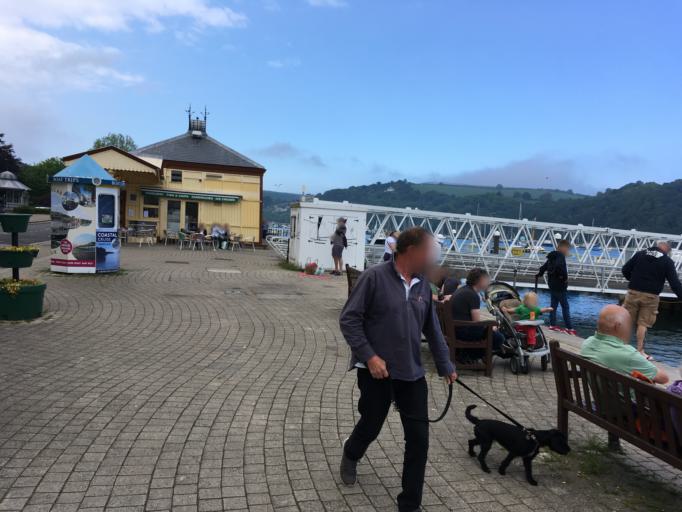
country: GB
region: England
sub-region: Devon
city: Dartmouth
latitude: 50.3510
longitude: -3.5773
